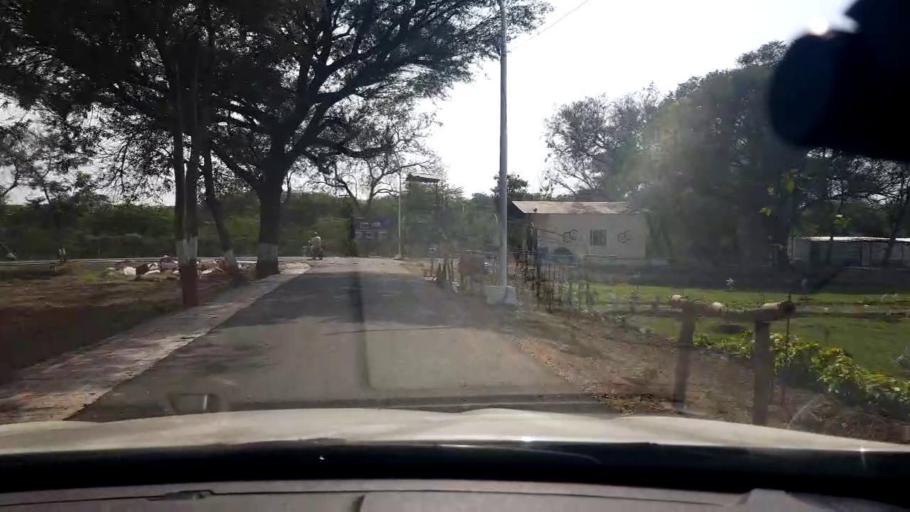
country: IN
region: Maharashtra
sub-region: Pune Division
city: Shivaji Nagar
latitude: 18.5402
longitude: 73.8559
